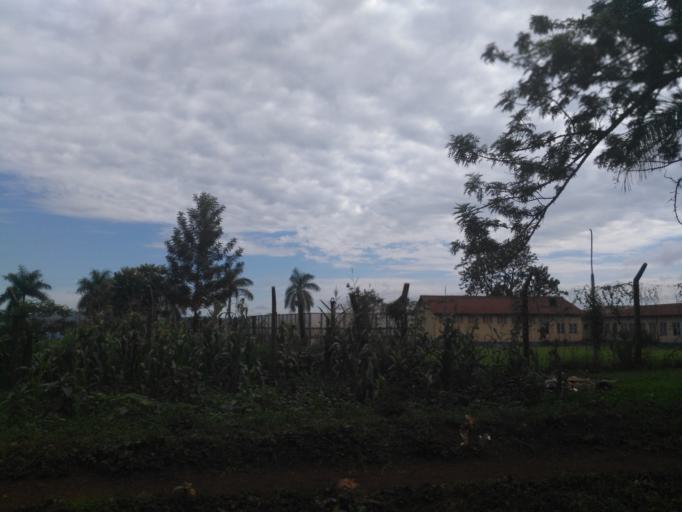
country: UG
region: Eastern Region
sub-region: Jinja District
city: Jinja
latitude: 0.4303
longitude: 33.1873
